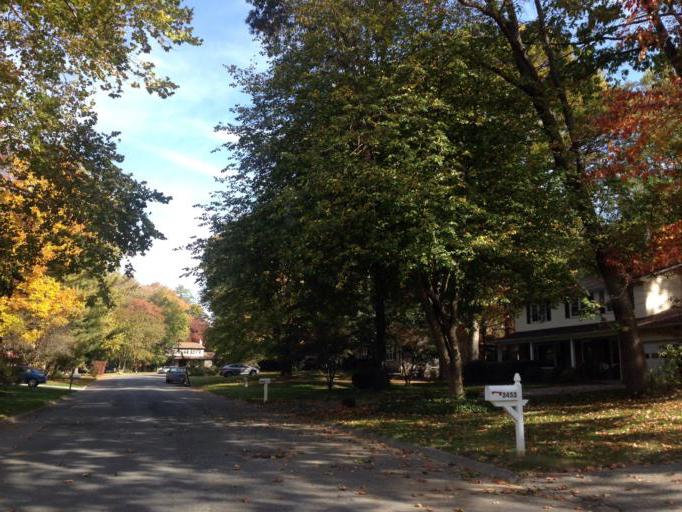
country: US
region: Maryland
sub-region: Howard County
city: Columbia
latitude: 39.2752
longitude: -76.8407
